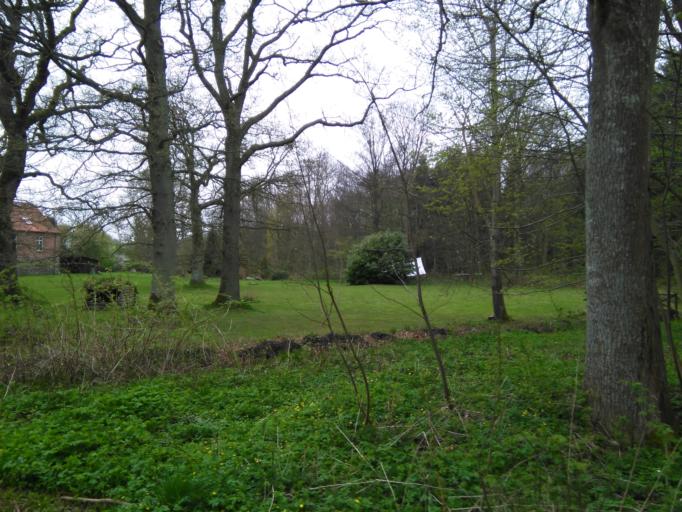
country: DK
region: Central Jutland
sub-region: Arhus Kommune
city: Beder
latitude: 56.0515
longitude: 10.2627
